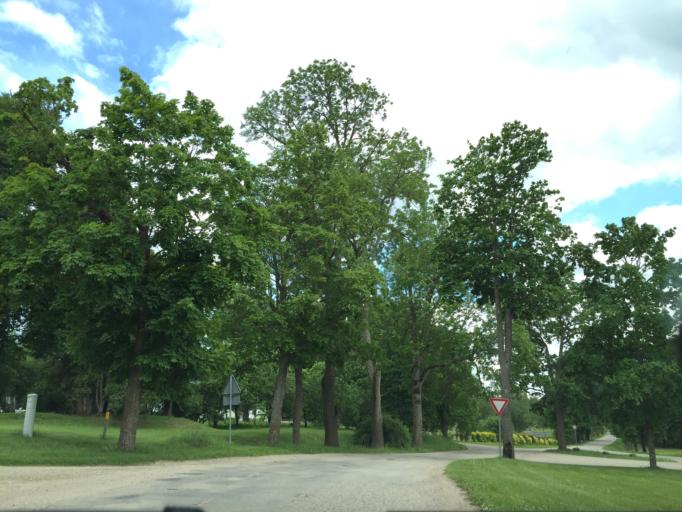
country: LV
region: Apes Novads
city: Ape
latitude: 57.5171
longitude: 26.4002
